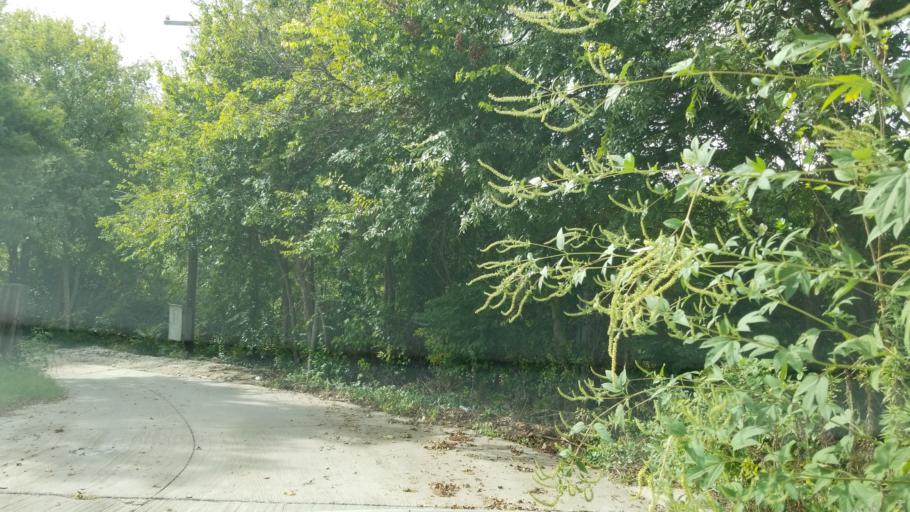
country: US
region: Texas
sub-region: Dallas County
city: Dallas
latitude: 32.7717
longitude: -96.7238
